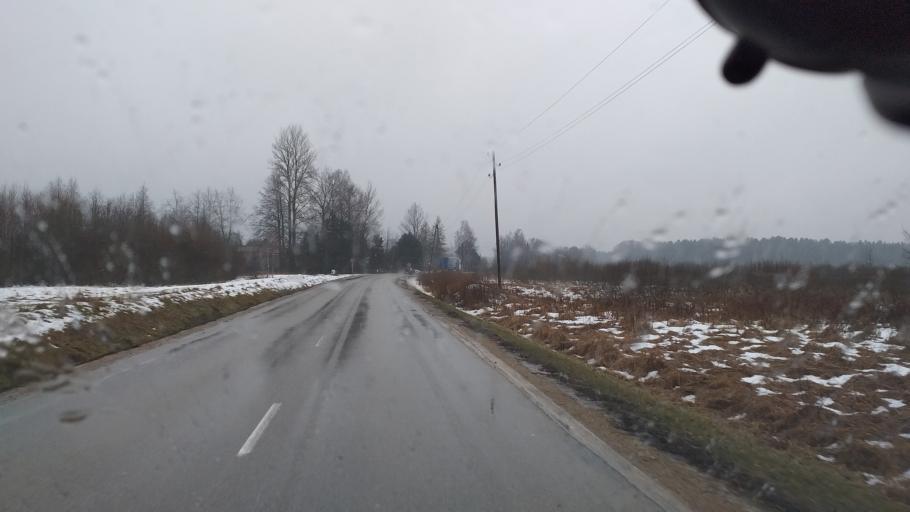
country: LV
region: Babite
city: Pinki
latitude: 56.9699
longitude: 23.9689
